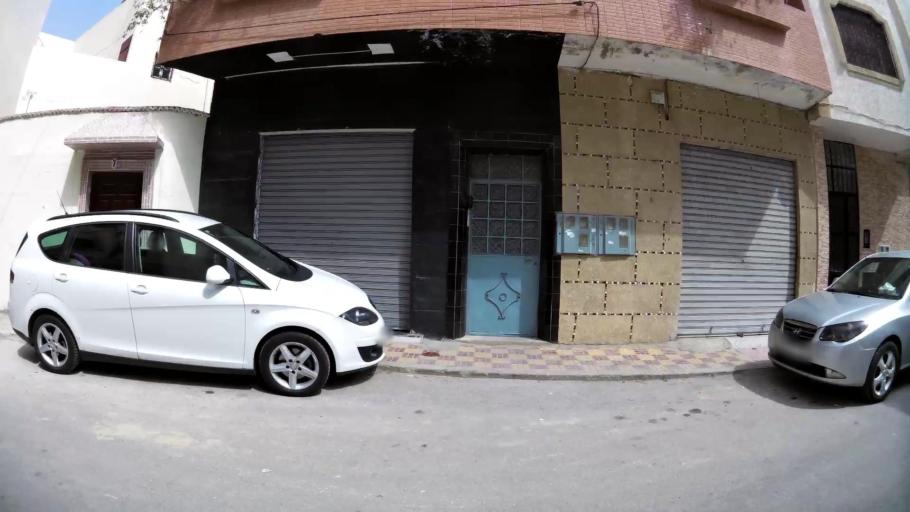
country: MA
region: Tanger-Tetouan
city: Tetouan
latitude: 35.5756
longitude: -5.3604
